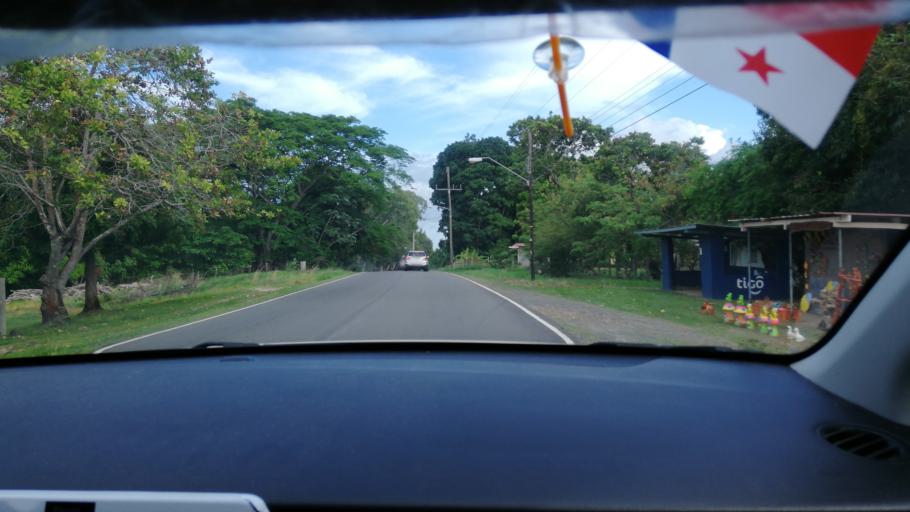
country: PA
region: Panama
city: Las Colinas
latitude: 8.5243
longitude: -80.0387
